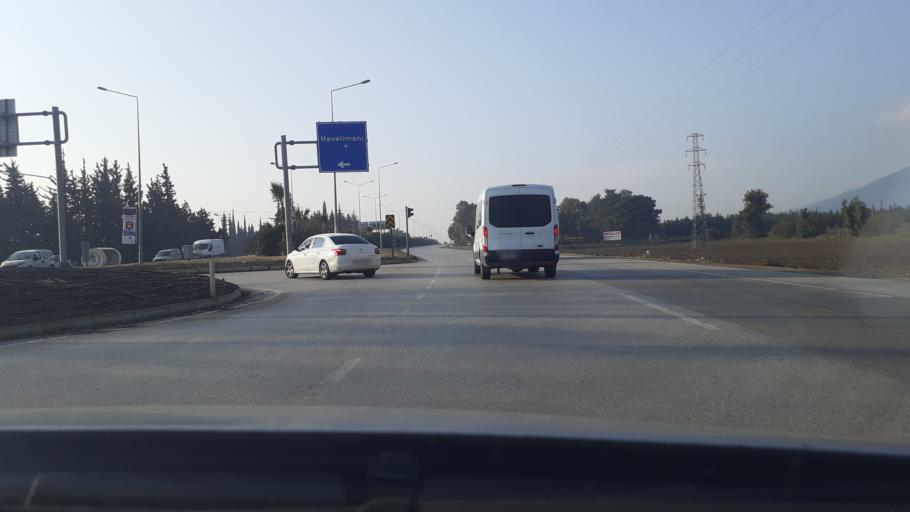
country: TR
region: Hatay
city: Serinyol
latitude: 36.3725
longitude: 36.2257
